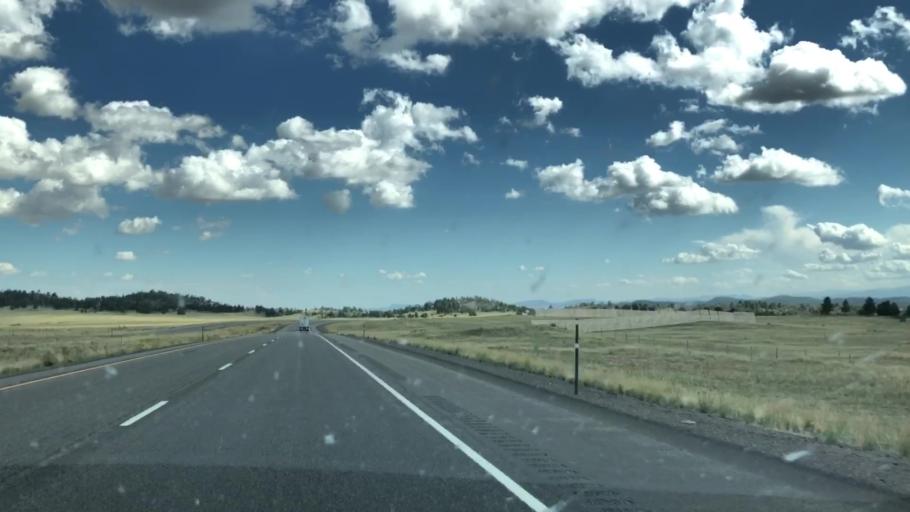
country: US
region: Wyoming
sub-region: Albany County
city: Laramie
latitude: 41.0229
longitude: -105.4248
